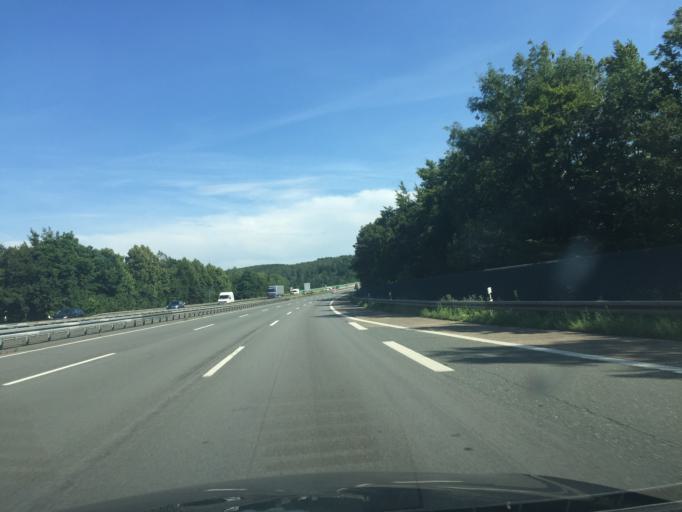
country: DE
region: North Rhine-Westphalia
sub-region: Regierungsbezirk Arnsberg
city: Siegen
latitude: 50.8326
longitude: 8.0414
